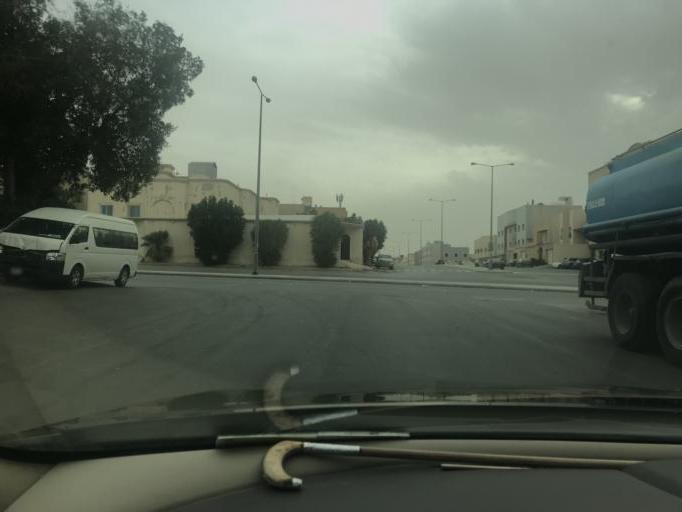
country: SA
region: Ar Riyad
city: Riyadh
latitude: 24.7860
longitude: 46.6946
